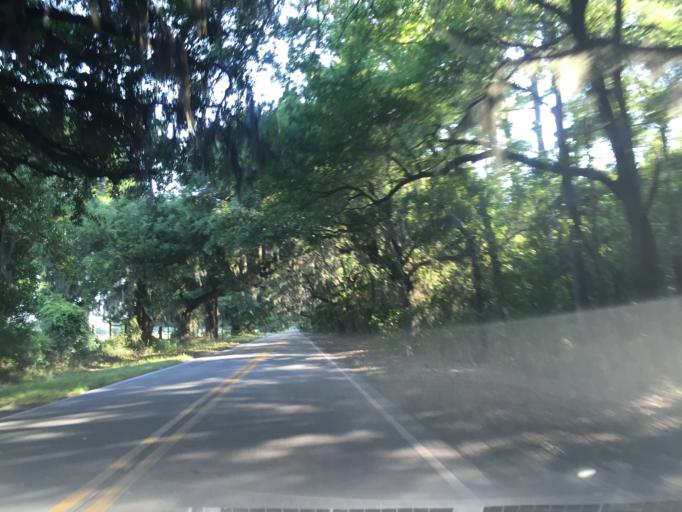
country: US
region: Georgia
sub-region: Chatham County
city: Isle of Hope
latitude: 31.9676
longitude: -81.0899
